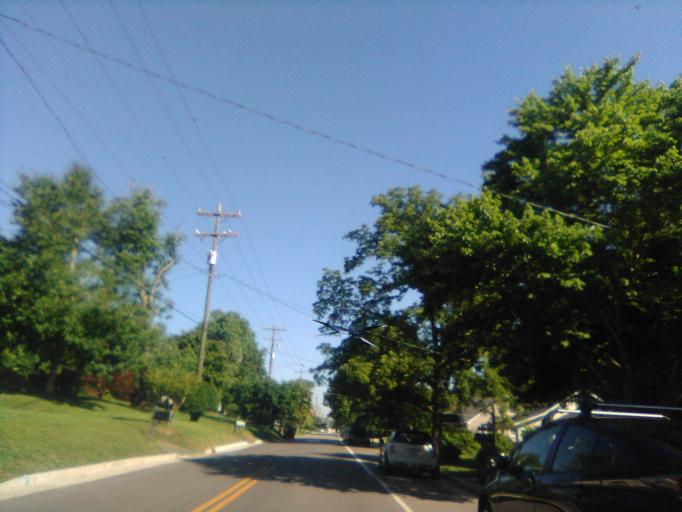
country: US
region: Tennessee
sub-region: Davidson County
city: Belle Meade
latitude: 36.1219
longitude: -86.8428
